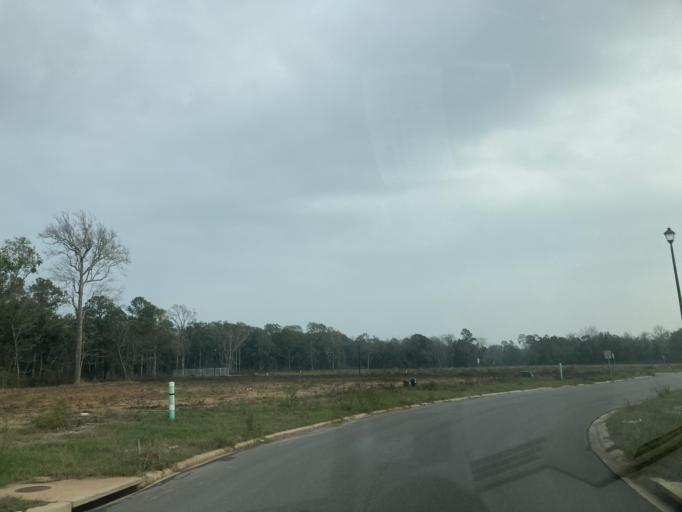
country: US
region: Mississippi
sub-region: Harrison County
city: Long Beach
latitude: 30.3779
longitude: -89.1592
